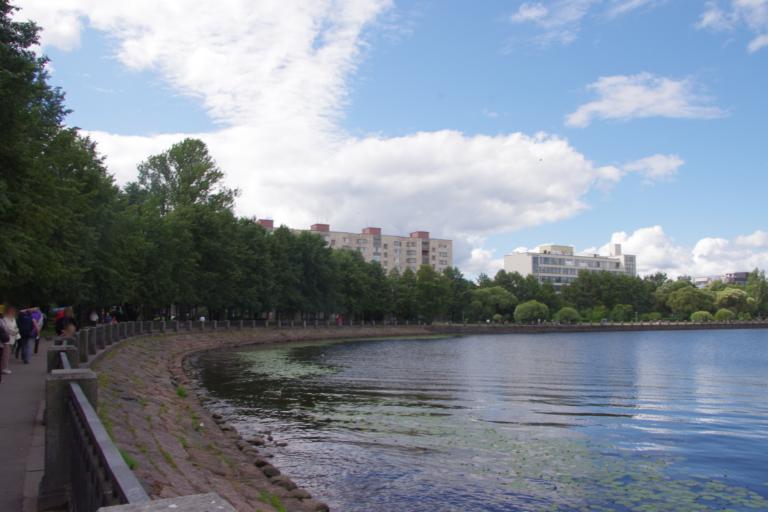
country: RU
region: Leningrad
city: Vyborg
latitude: 60.7137
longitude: 28.7473
